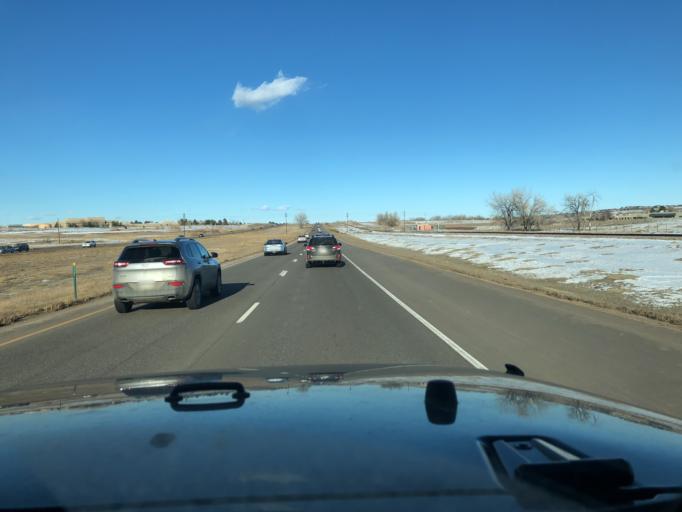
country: US
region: Colorado
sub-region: Boulder County
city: Gunbarrel
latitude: 40.0772
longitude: -105.2033
